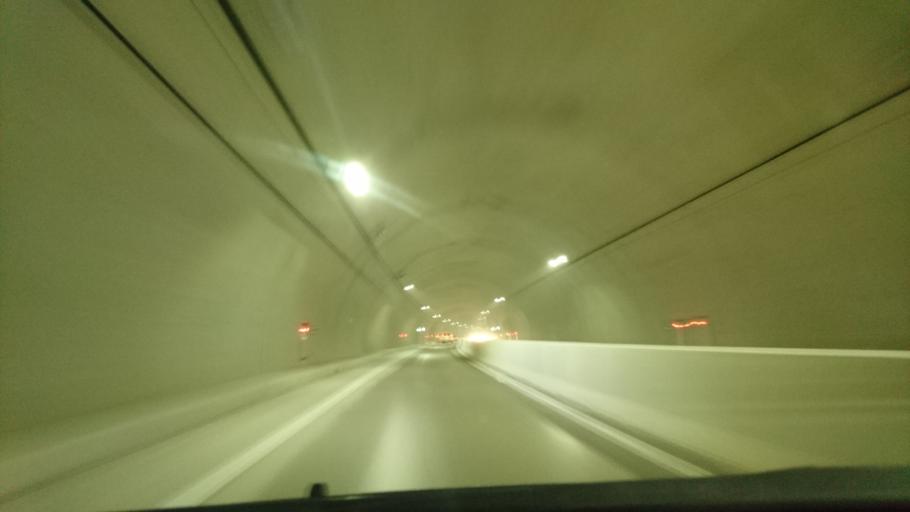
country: JP
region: Iwate
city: Ofunato
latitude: 38.9724
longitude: 141.6238
